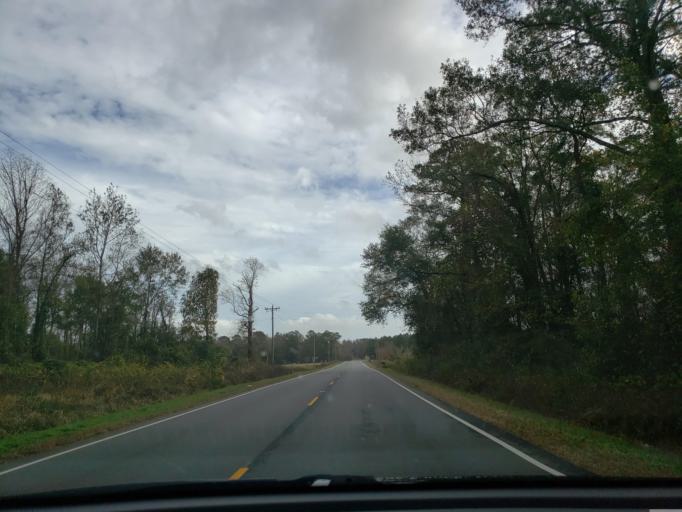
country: US
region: North Carolina
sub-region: Duplin County
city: Beulaville
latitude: 34.8356
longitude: -77.8569
